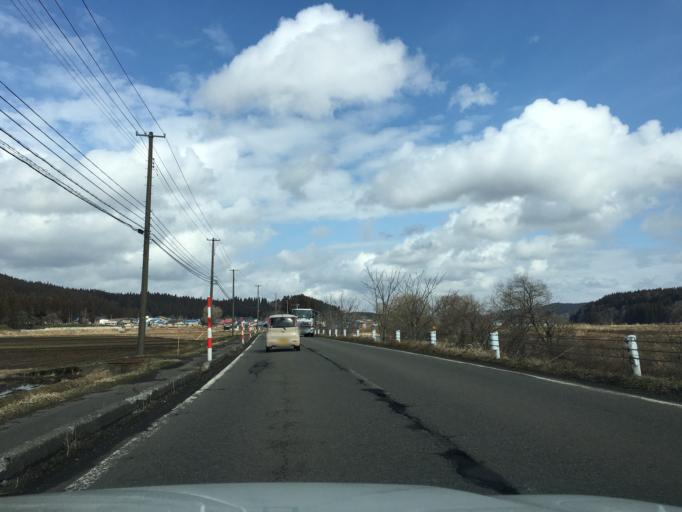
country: JP
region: Akita
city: Takanosu
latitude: 40.0392
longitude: 140.2790
